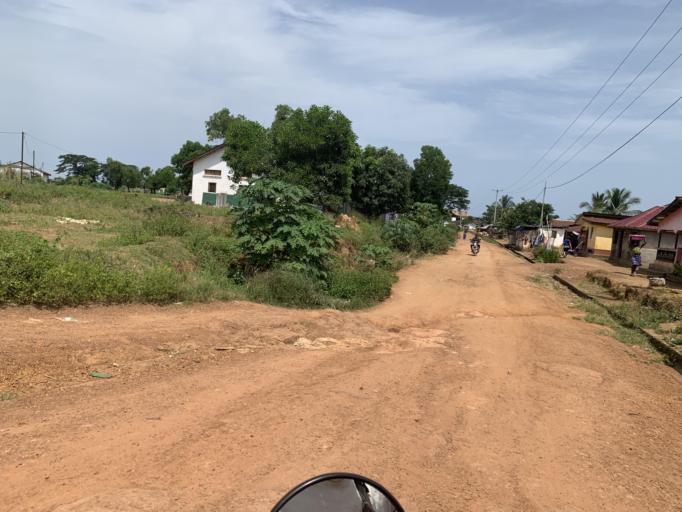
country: SL
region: Western Area
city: Hastings
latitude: 8.4108
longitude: -13.1305
